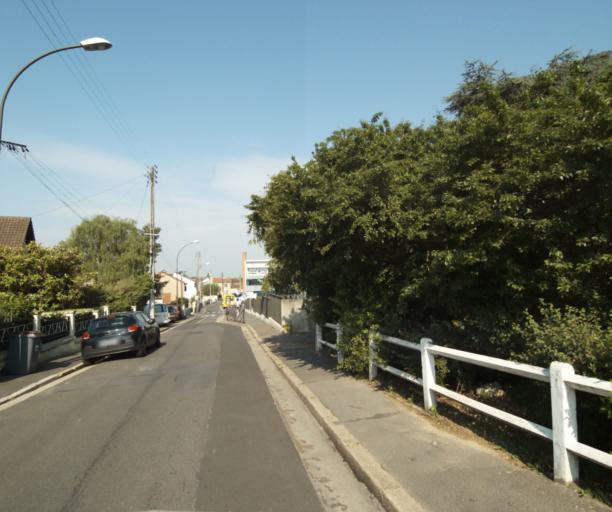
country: FR
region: Ile-de-France
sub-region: Departement du Val-d'Oise
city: Sannois
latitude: 48.9605
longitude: 2.2463
